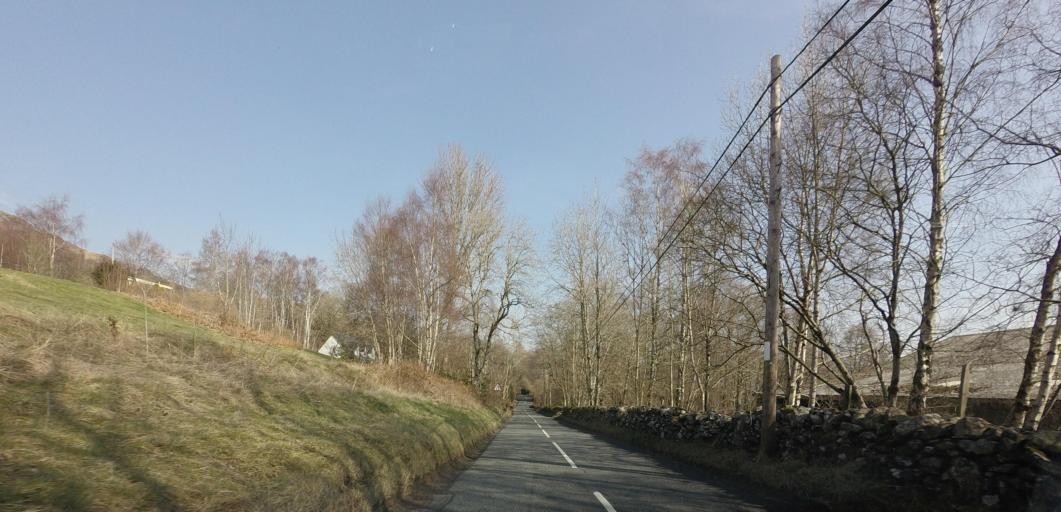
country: GB
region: Scotland
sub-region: Stirling
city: Callander
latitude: 56.4864
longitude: -4.2830
